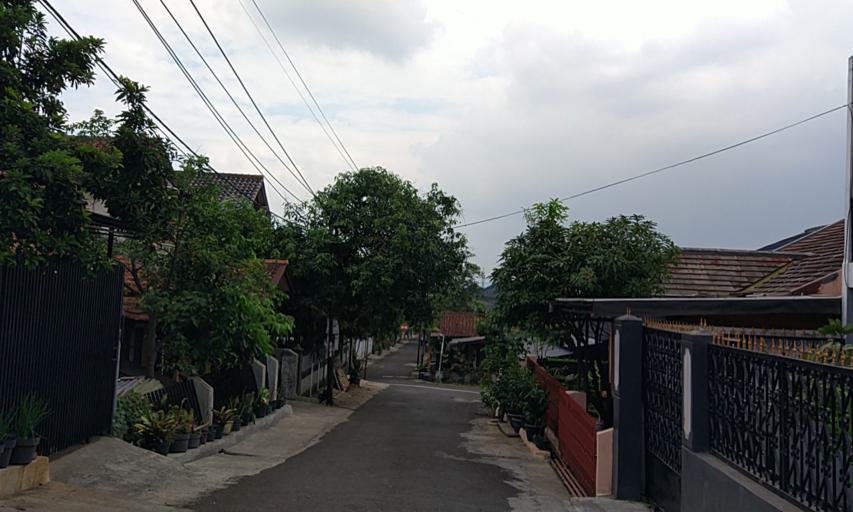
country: ID
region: West Java
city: Cileunyi
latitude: -6.9032
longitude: 107.6927
